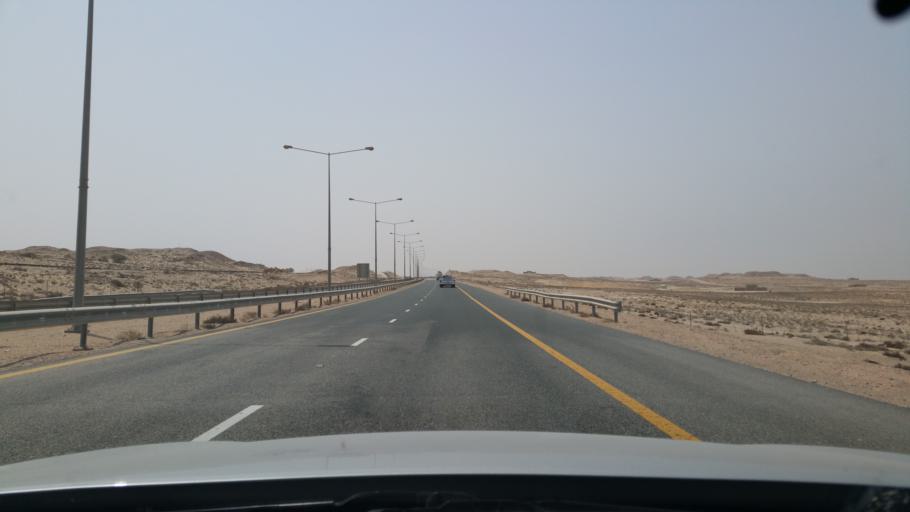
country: QA
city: Umm Bab
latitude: 25.2569
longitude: 50.7965
